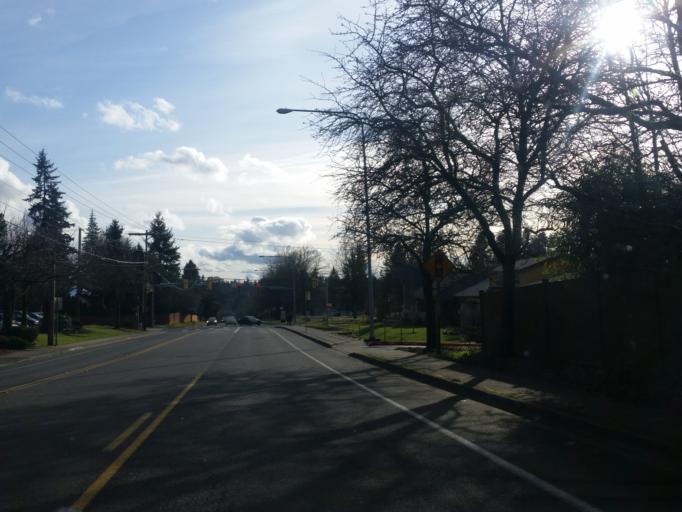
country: US
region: Washington
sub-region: King County
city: Kingsgate
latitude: 47.7197
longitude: -122.1643
